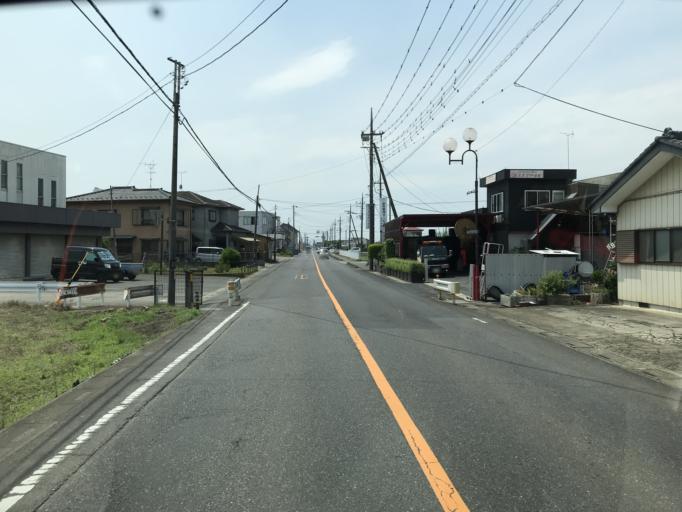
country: JP
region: Saitama
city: Satte
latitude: 36.0757
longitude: 139.7451
